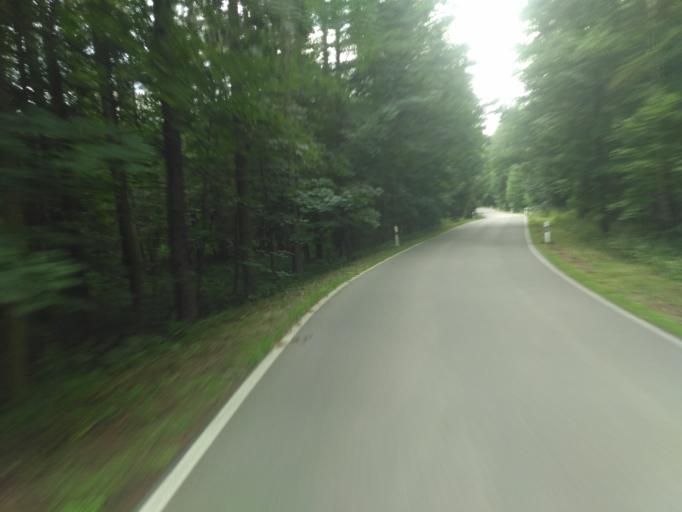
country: DE
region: Saxony
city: Kurort Gohrisch
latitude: 50.8976
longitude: 14.1127
